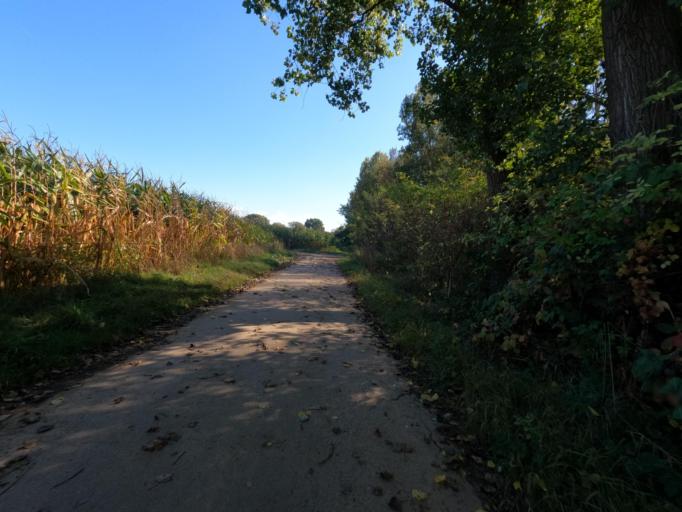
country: DE
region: North Rhine-Westphalia
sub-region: Regierungsbezirk Koln
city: Linnich
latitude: 51.0155
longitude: 6.2629
